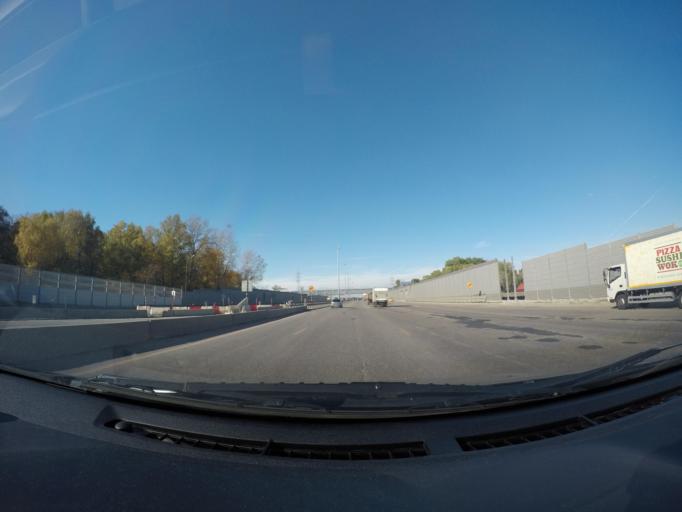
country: RU
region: Moskovskaya
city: Tomilino
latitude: 55.6316
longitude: 37.9377
